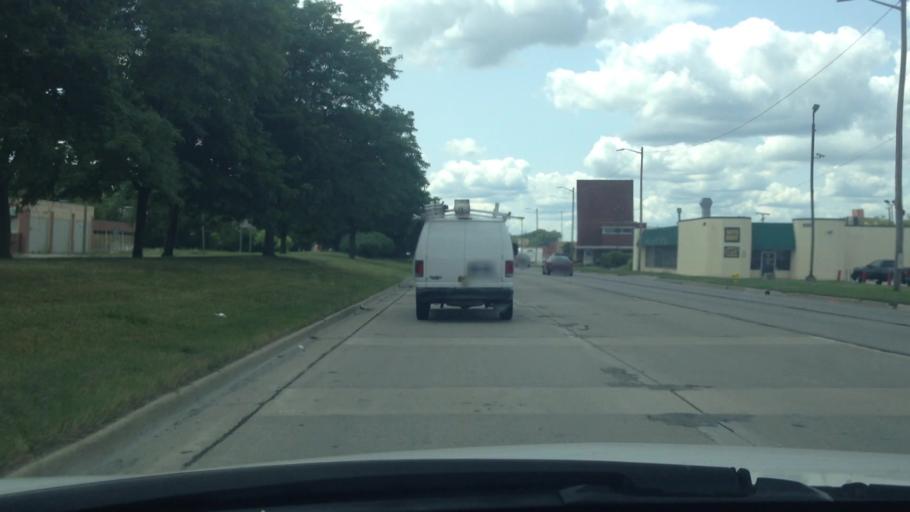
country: US
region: Michigan
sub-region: Wayne County
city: Inkster
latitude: 42.2952
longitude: -83.3039
